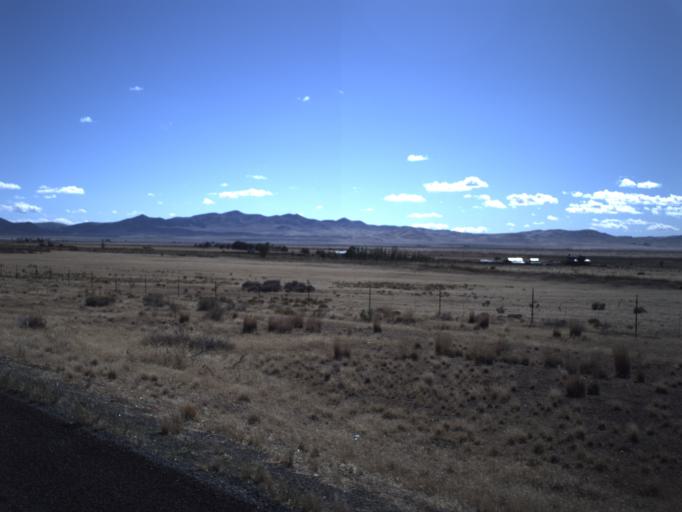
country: US
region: Utah
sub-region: Beaver County
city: Milford
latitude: 38.2851
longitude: -112.9656
